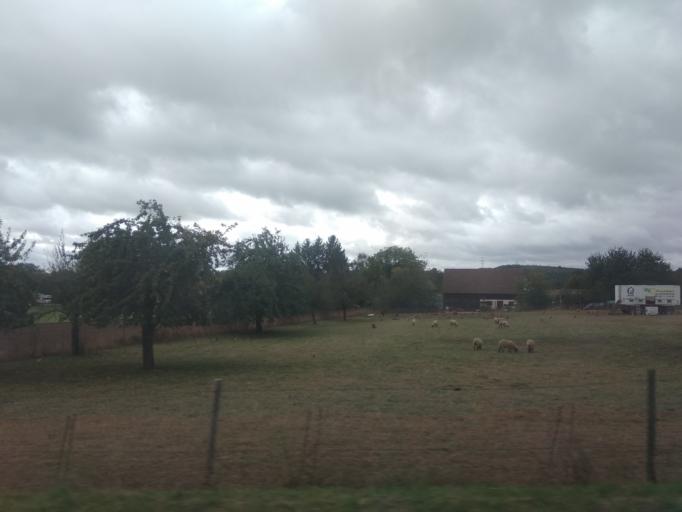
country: DE
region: Baden-Wuerttemberg
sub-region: Karlsruhe Region
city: Mosbach
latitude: 49.3483
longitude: 9.1755
